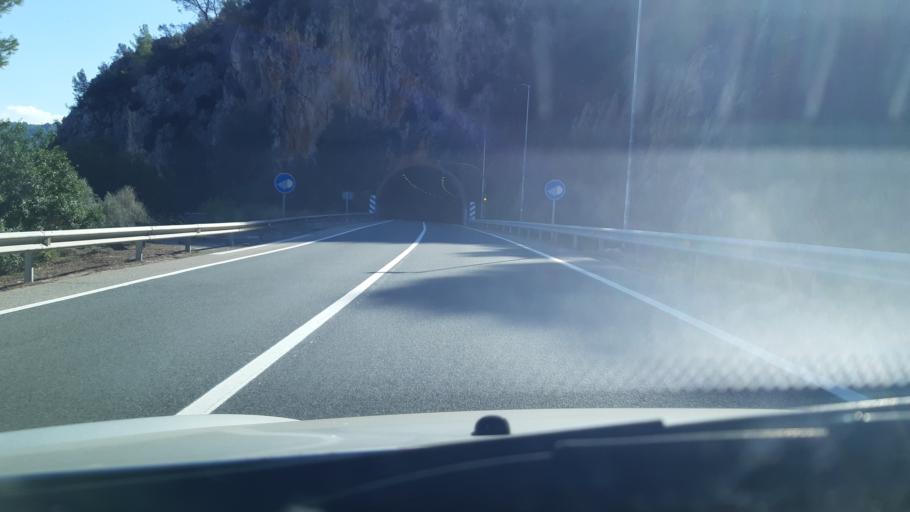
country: ES
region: Catalonia
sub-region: Provincia de Tarragona
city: Benifallet
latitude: 40.9512
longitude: 0.4832
